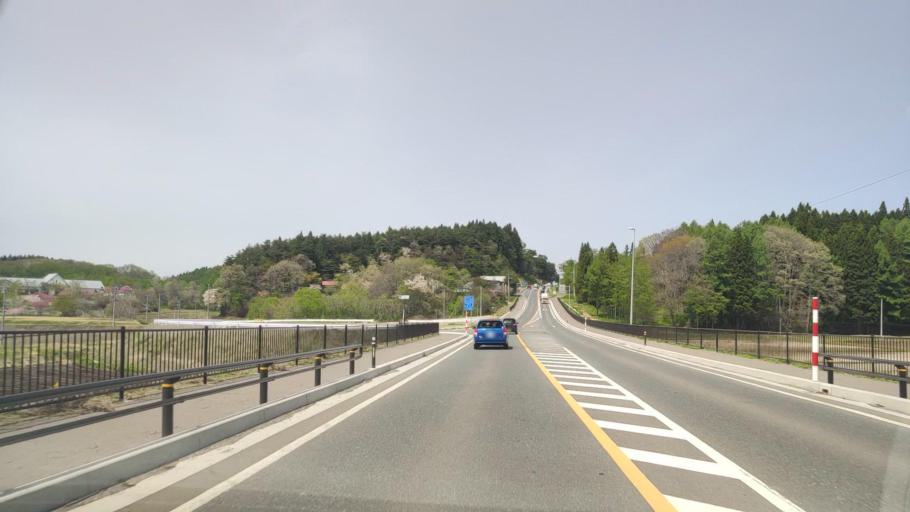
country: JP
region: Aomori
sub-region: Misawa Shi
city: Inuotose
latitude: 40.6637
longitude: 141.1876
